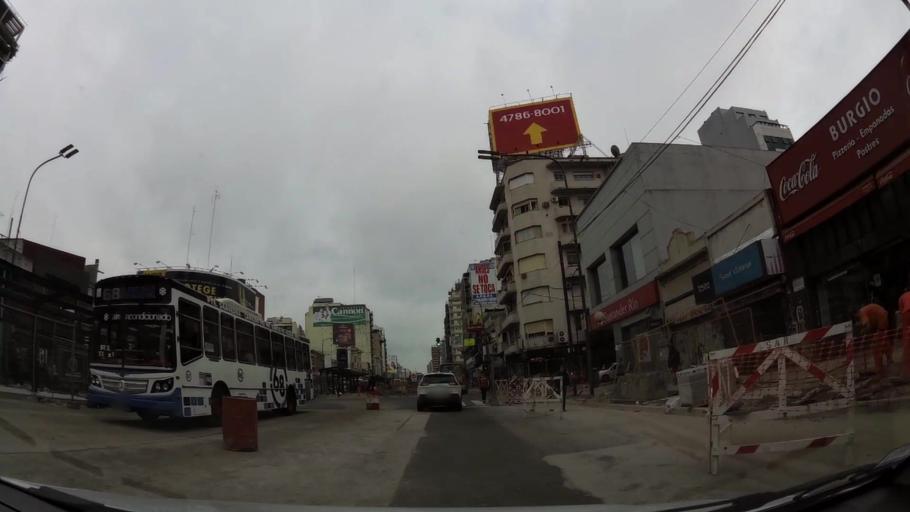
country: AR
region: Buenos Aires F.D.
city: Colegiales
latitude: -34.5584
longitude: -58.4596
